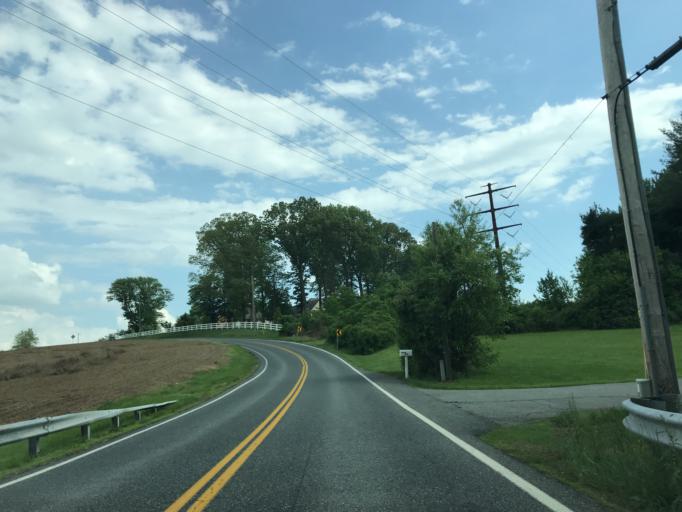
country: US
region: Pennsylvania
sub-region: York County
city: Susquehanna Trails
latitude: 39.6773
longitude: -76.3887
